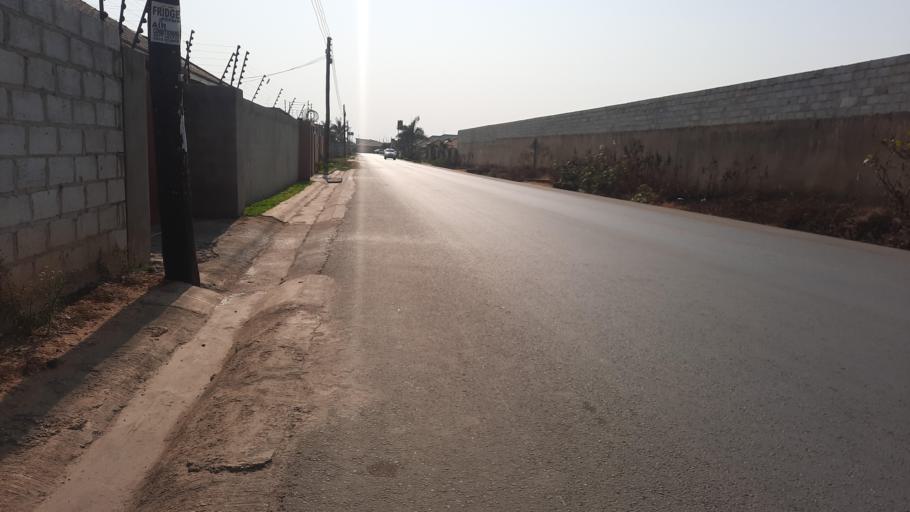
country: ZM
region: Lusaka
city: Lusaka
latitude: -15.3901
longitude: 28.3874
